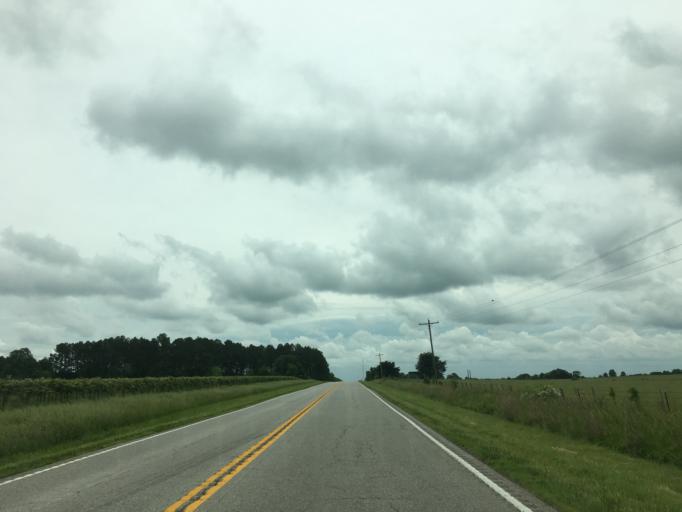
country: US
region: Missouri
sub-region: Gasconade County
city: Owensville
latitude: 38.5089
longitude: -91.4618
